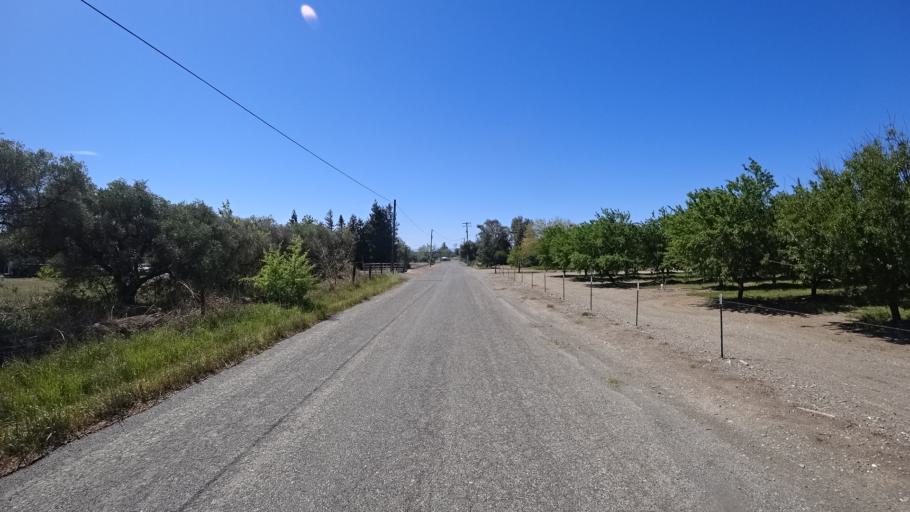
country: US
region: California
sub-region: Glenn County
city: Orland
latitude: 39.7418
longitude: -122.1749
